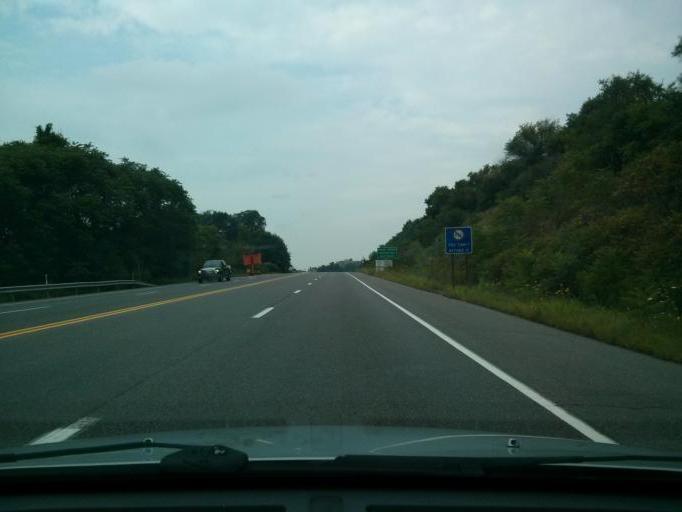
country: US
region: Pennsylvania
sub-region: Centre County
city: State College
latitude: 40.8042
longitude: -77.8457
